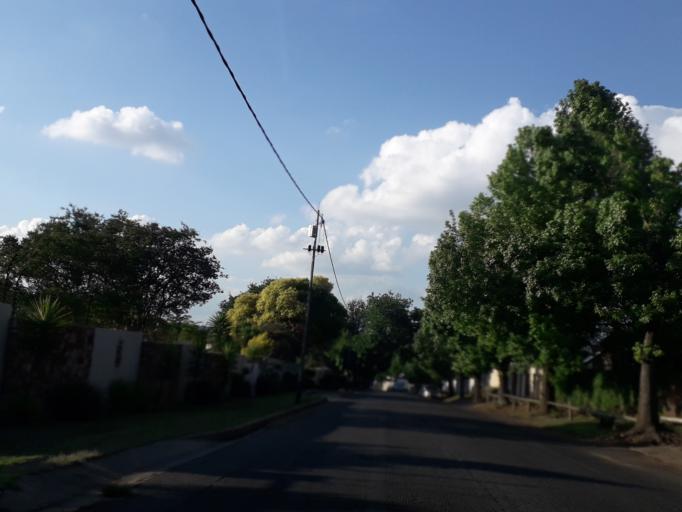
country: ZA
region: Gauteng
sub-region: City of Johannesburg Metropolitan Municipality
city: Johannesburg
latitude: -26.1485
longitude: 28.0065
